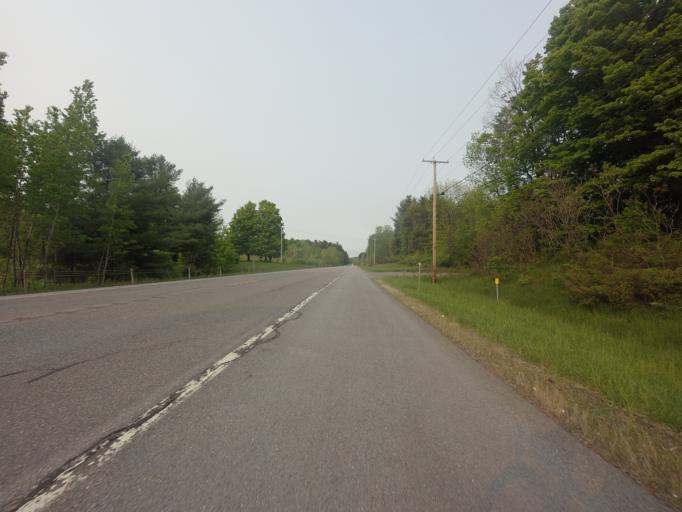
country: US
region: New York
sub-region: St. Lawrence County
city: Gouverneur
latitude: 44.1087
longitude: -75.4033
